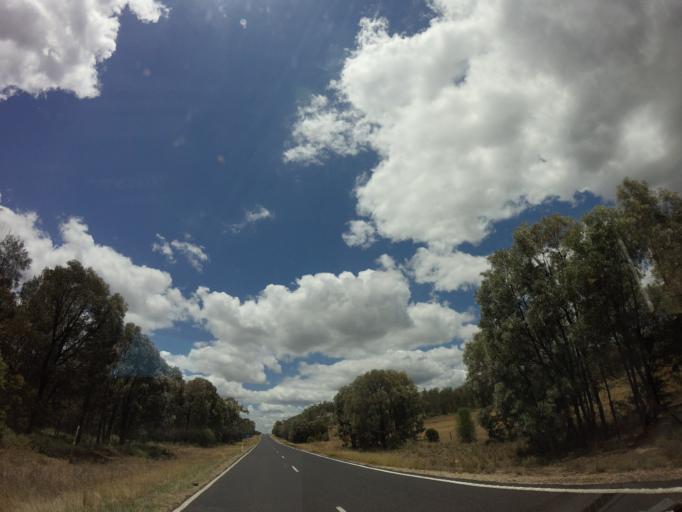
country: AU
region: Queensland
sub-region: Goondiwindi
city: Goondiwindi
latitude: -28.0361
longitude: 150.8137
